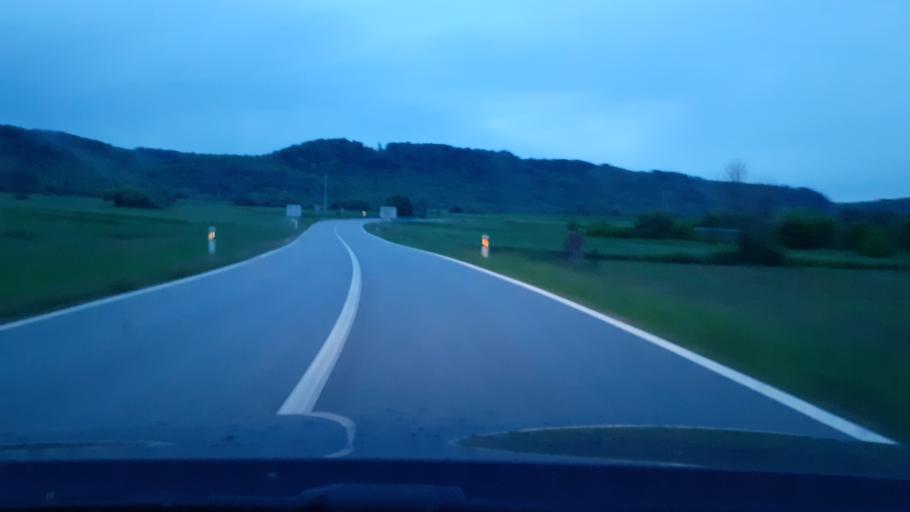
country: HR
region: Pozesko-Slavonska
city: Bilice
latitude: 45.2317
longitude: 17.8470
